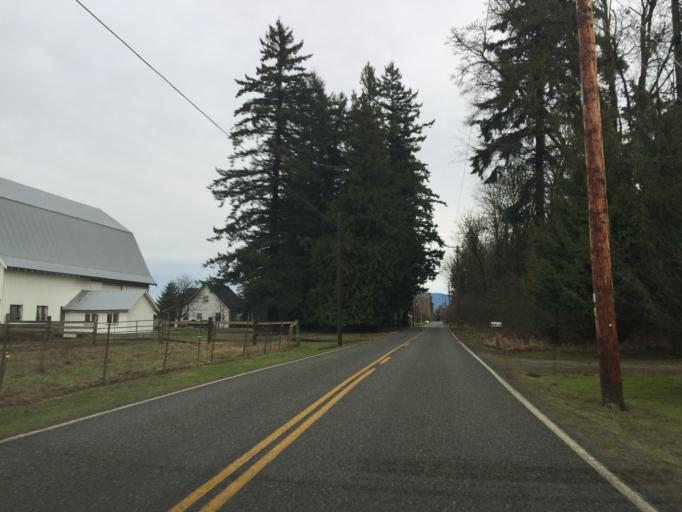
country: US
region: Washington
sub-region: Whatcom County
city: Lynden
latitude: 48.9061
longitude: -122.5122
